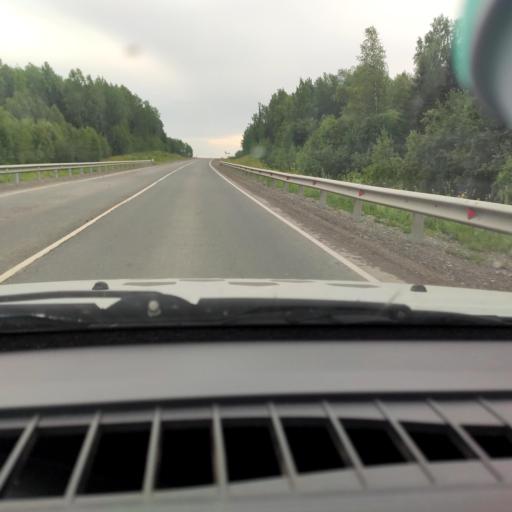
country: RU
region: Kirov
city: Kostino
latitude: 58.8335
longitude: 53.5006
